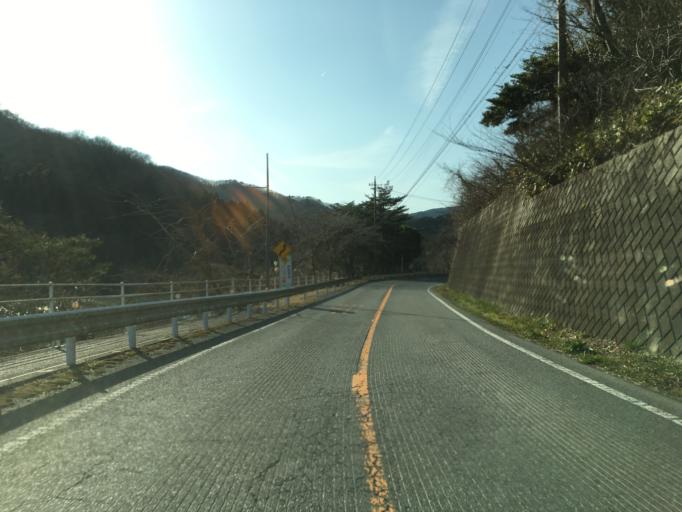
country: JP
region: Ibaraki
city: Takahagi
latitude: 36.7250
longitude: 140.6464
